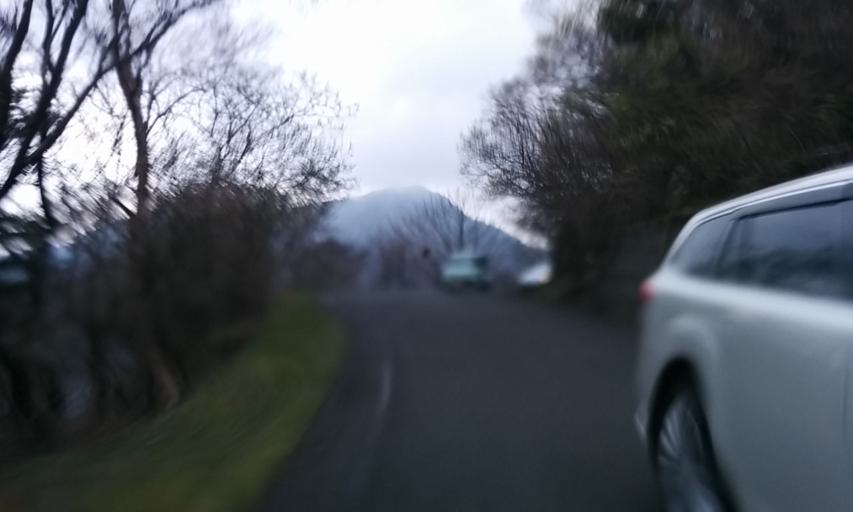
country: JP
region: Ehime
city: Saijo
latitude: 33.7891
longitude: 133.2084
